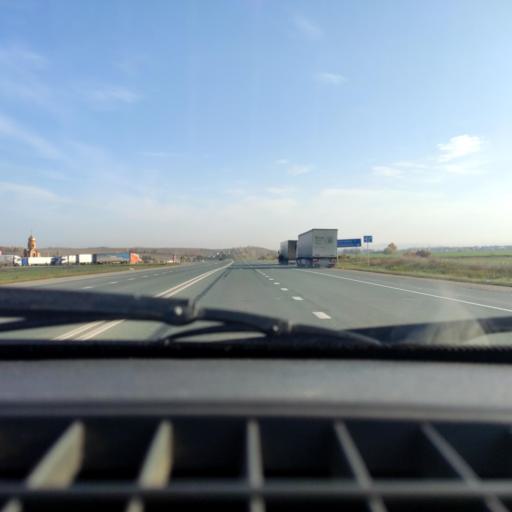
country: RU
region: Bashkortostan
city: Avdon
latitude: 54.6962
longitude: 55.7597
